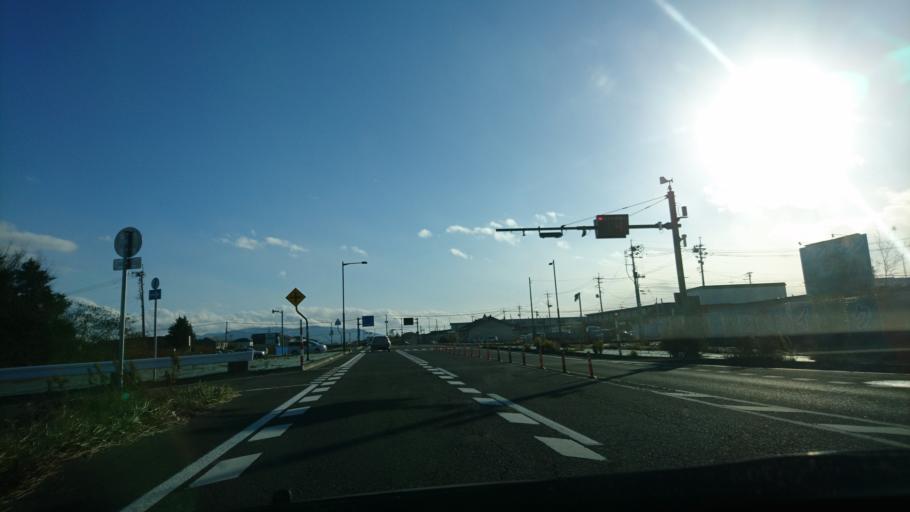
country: JP
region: Iwate
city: Mizusawa
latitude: 39.1377
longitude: 141.1627
